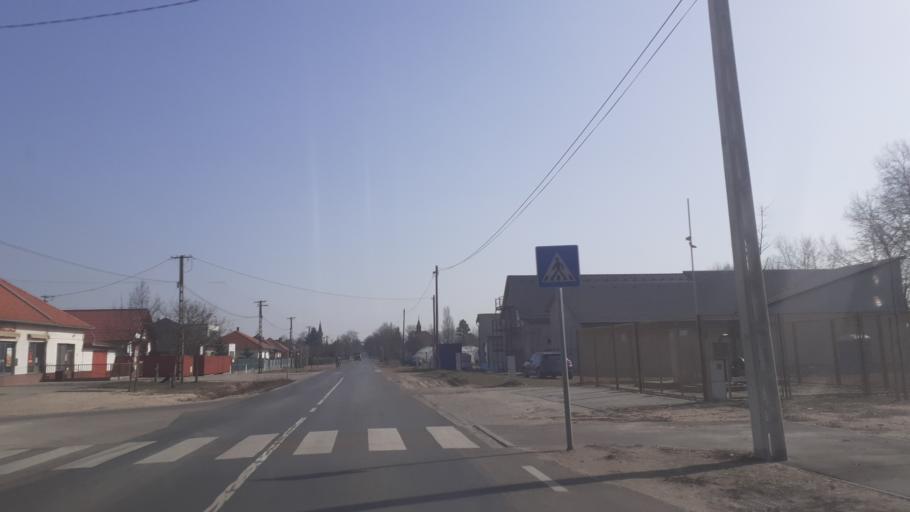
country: HU
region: Bacs-Kiskun
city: Lajosmizse
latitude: 46.9783
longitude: 19.5725
